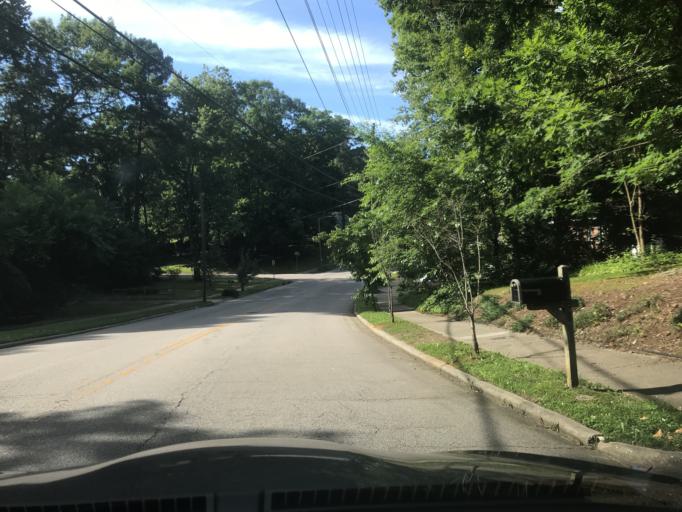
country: US
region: North Carolina
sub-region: Wake County
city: Raleigh
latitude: 35.8272
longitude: -78.6012
